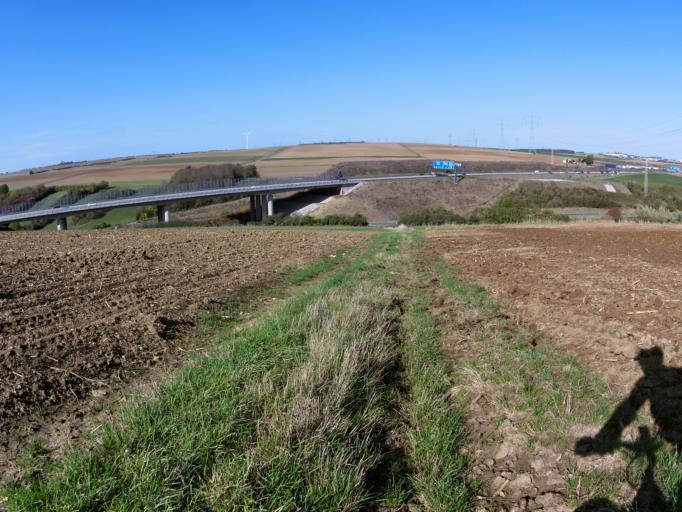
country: DE
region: Bavaria
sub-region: Regierungsbezirk Unterfranken
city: Theilheim
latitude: 49.7540
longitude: 10.0517
